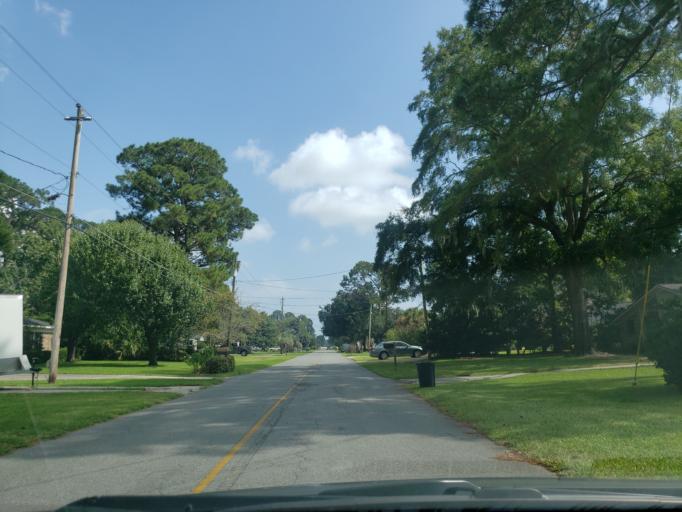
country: US
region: Georgia
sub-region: Chatham County
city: Montgomery
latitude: 31.9317
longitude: -81.0900
